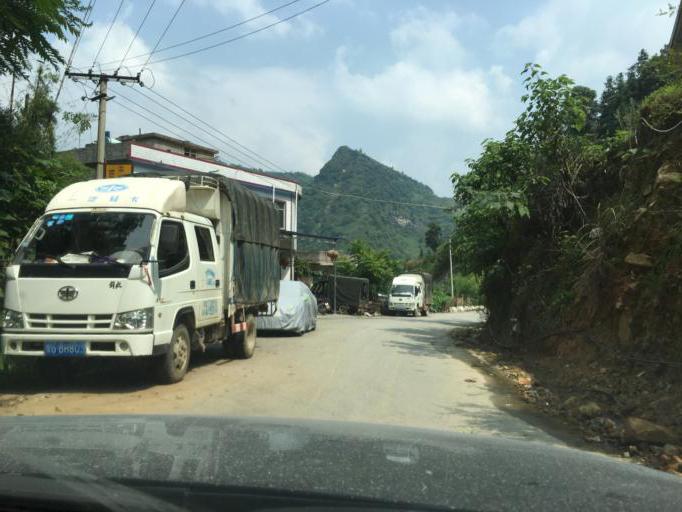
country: CN
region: Guangxi Zhuangzu Zizhiqu
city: Tongle
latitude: 25.2945
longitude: 106.2669
